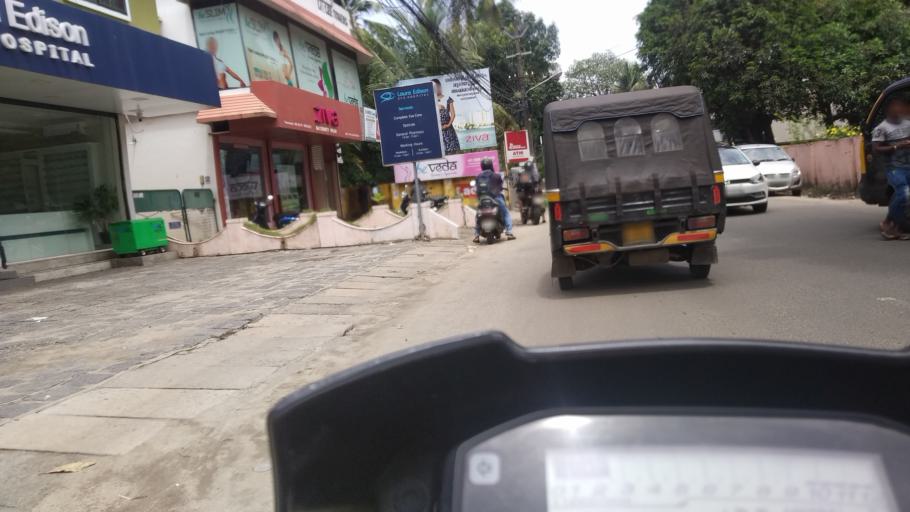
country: IN
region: Kerala
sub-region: Ernakulam
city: Cochin
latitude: 9.9901
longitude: 76.3098
